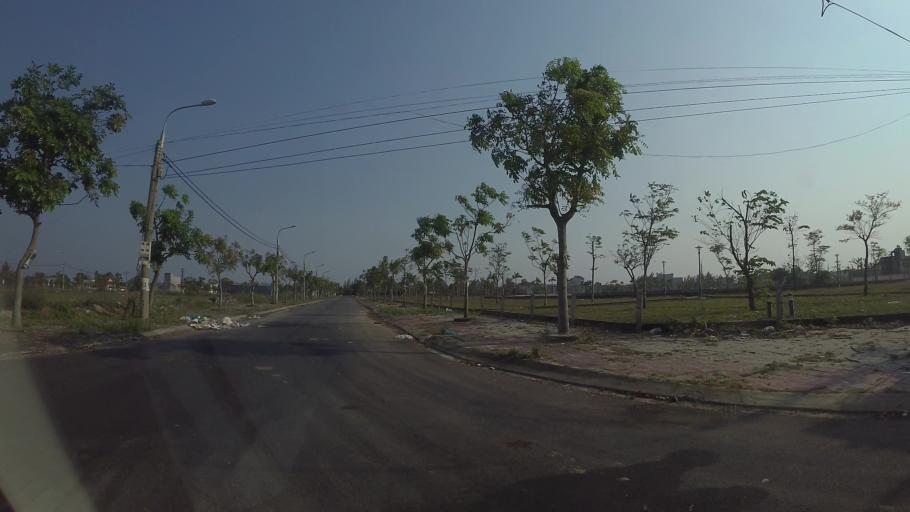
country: VN
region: Da Nang
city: Ngu Hanh Son
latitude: 15.9612
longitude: 108.2585
